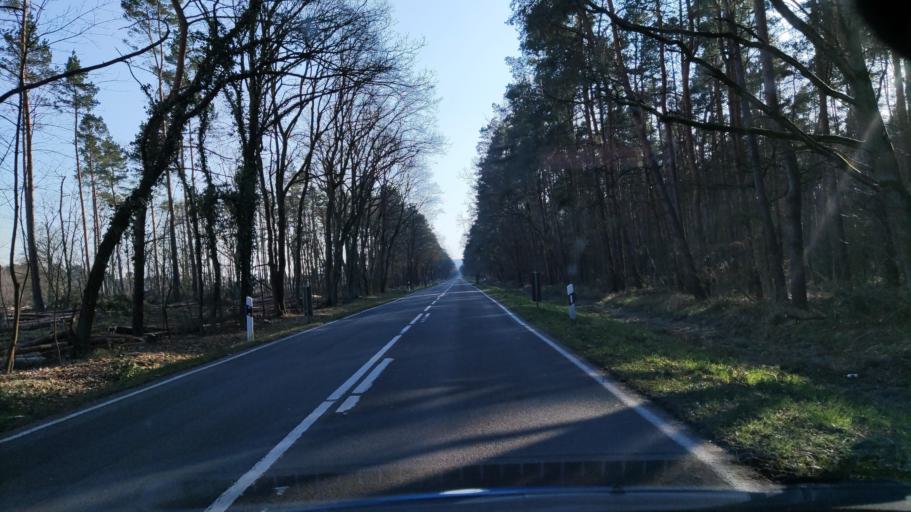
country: DE
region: Saxony-Anhalt
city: Seehausen
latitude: 52.8724
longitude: 11.7411
